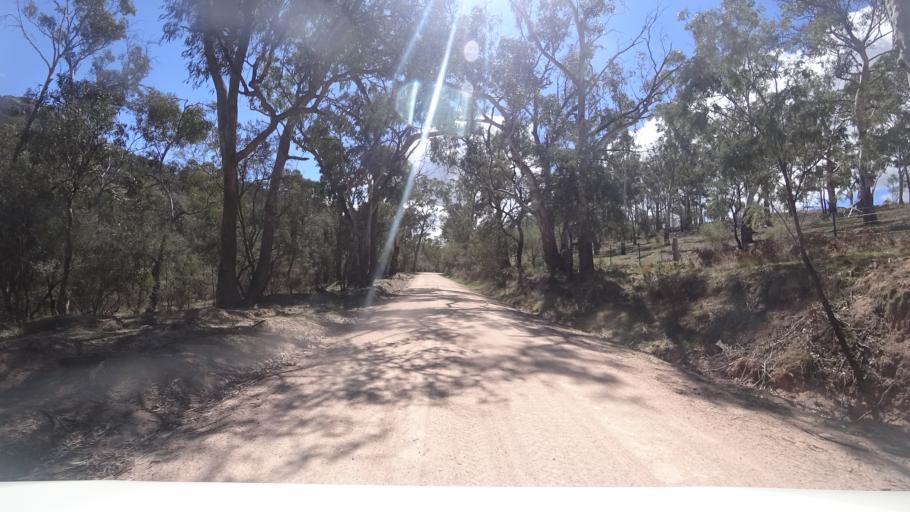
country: AU
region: New South Wales
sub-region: Oberon
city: Oberon
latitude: -33.5450
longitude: 149.9322
